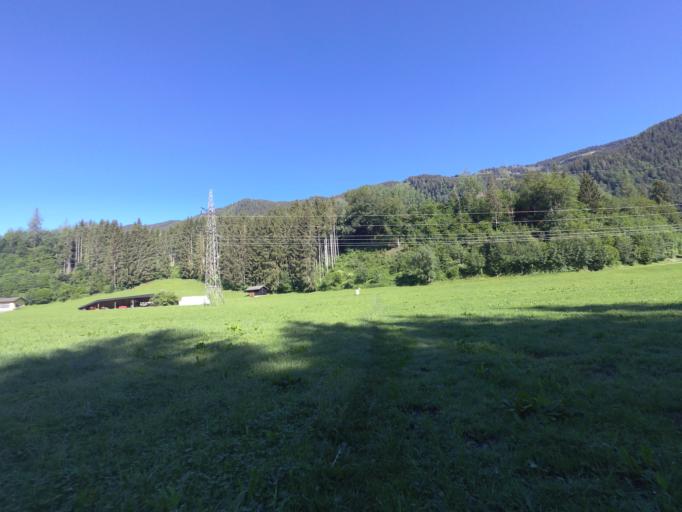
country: AT
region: Salzburg
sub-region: Politischer Bezirk Sankt Johann im Pongau
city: Goldegg
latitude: 47.3256
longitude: 13.0815
